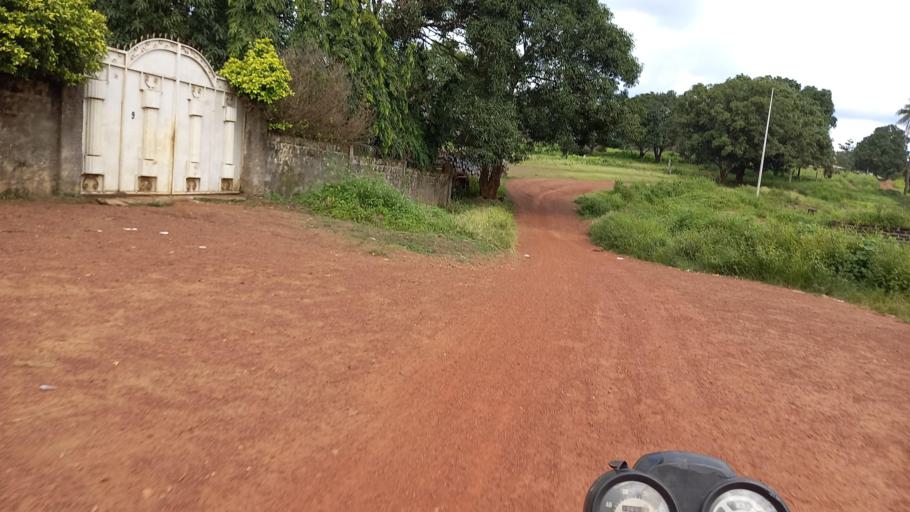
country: SL
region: Northern Province
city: Kamakwie
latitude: 9.5038
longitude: -12.2395
